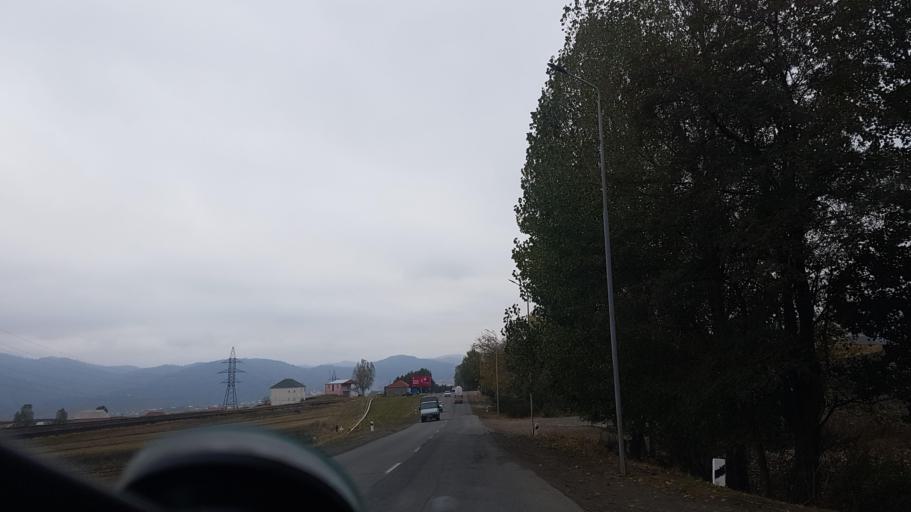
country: AZ
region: Gadabay Rayon
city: Ariqdam
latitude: 40.6089
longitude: 45.8126
